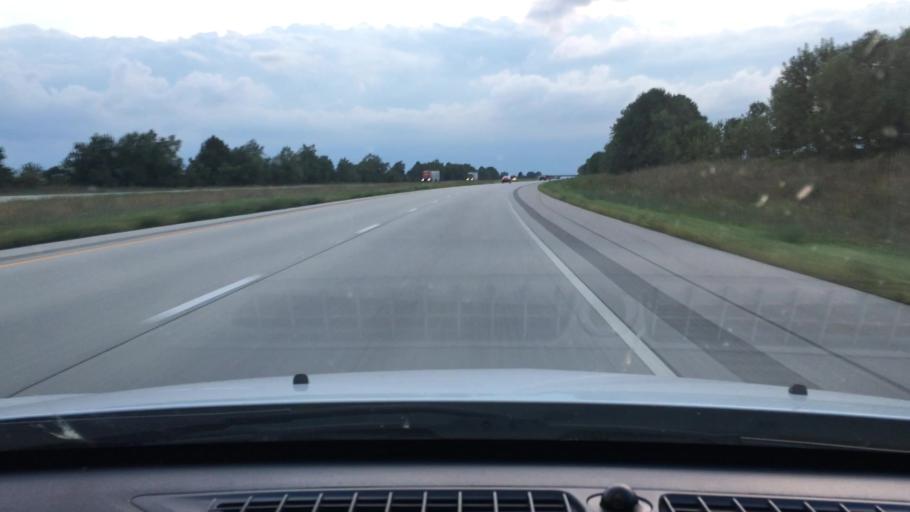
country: US
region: Illinois
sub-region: Sangamon County
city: New Berlin
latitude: 39.7416
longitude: -89.8271
